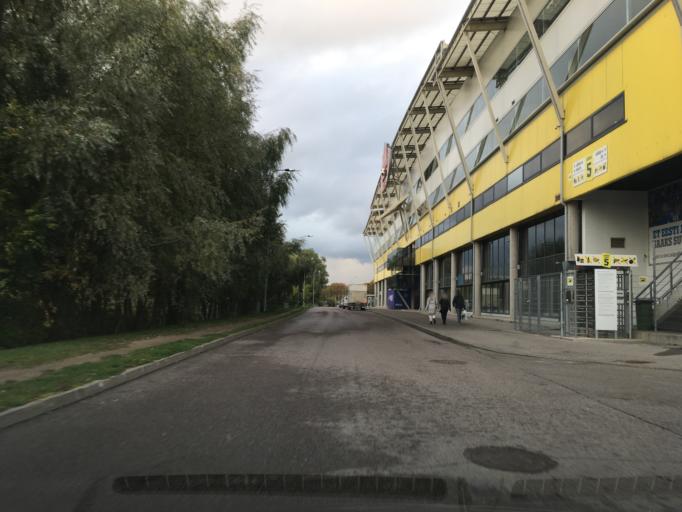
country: EE
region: Harju
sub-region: Tallinna linn
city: Tallinn
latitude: 59.4205
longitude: 24.7313
